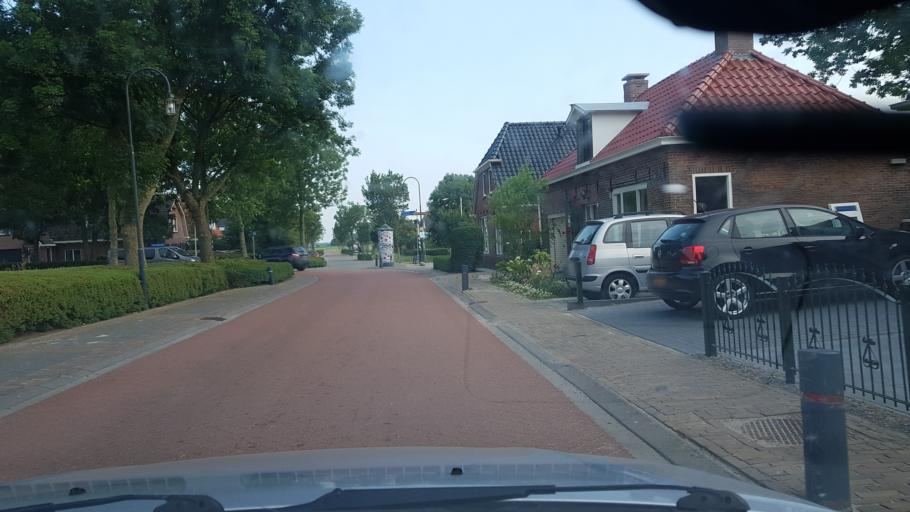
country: NL
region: Friesland
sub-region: Gemeente Ferwerderadiel
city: Burdaard
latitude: 53.3229
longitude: 5.8742
